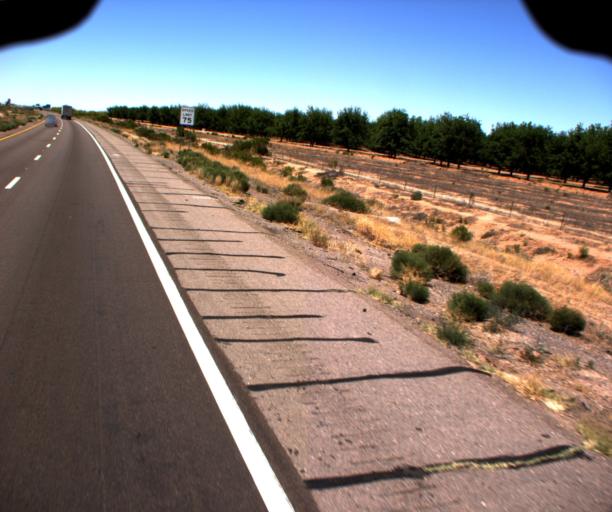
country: US
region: Arizona
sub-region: Pinal County
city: Eloy
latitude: 32.7285
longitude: -111.5262
